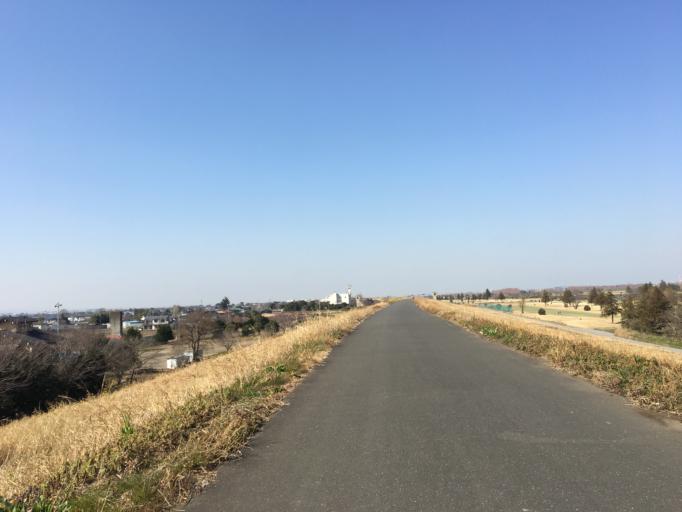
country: JP
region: Saitama
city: Shiki
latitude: 35.8656
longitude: 139.5765
